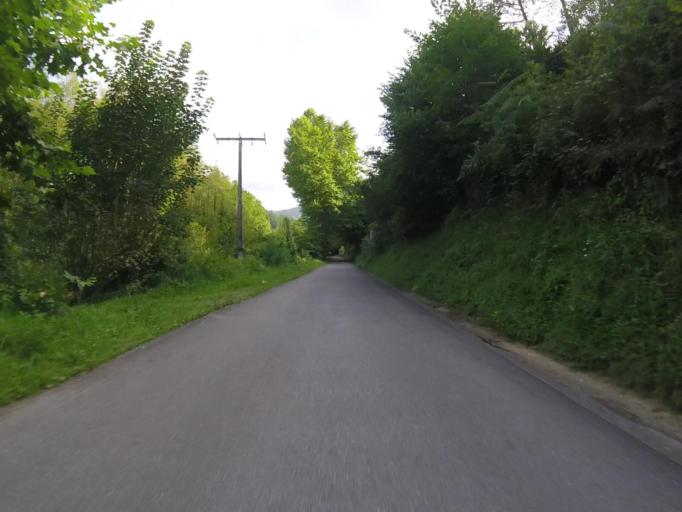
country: ES
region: Basque Country
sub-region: Provincia de Guipuzcoa
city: Astigarraga
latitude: 43.2540
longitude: -1.9501
